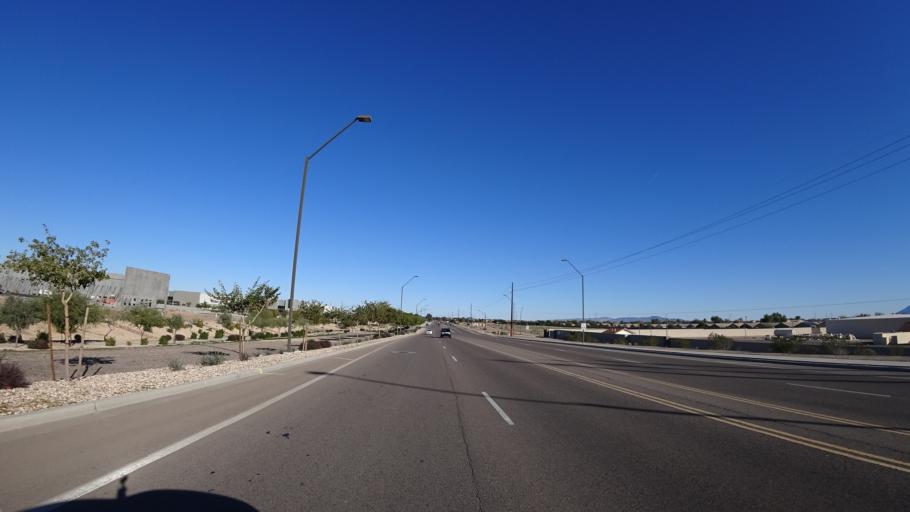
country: US
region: Arizona
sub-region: Maricopa County
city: Avondale
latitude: 33.4497
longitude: -112.3305
